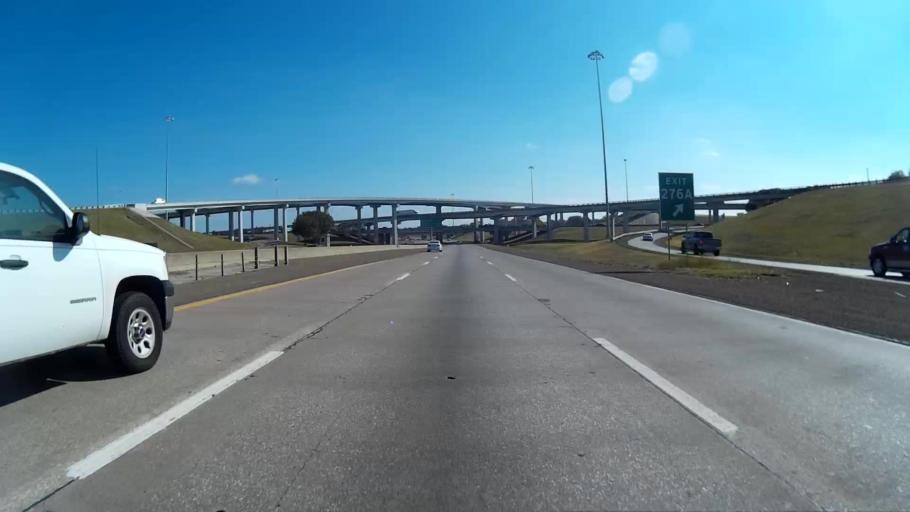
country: US
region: Texas
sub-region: Dallas County
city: Hutchins
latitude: 32.6634
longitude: -96.7283
